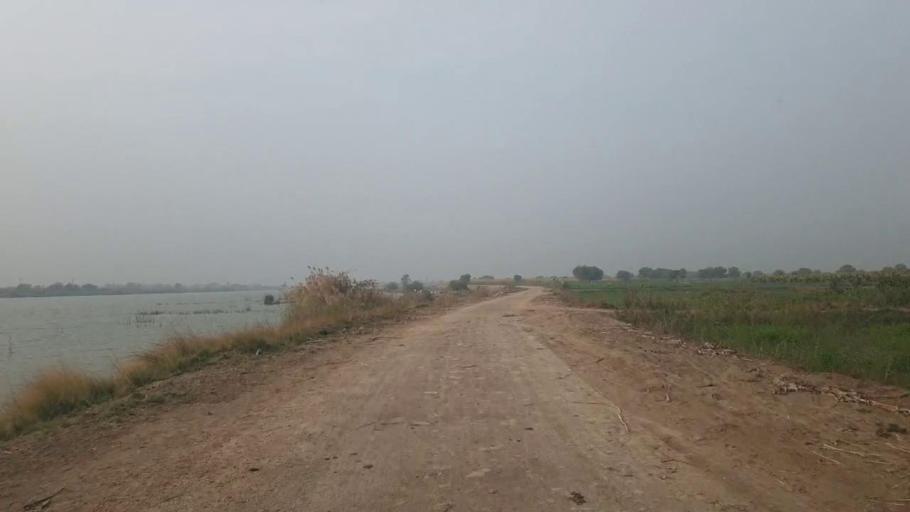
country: PK
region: Sindh
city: Berani
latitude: 25.8158
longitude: 68.7383
